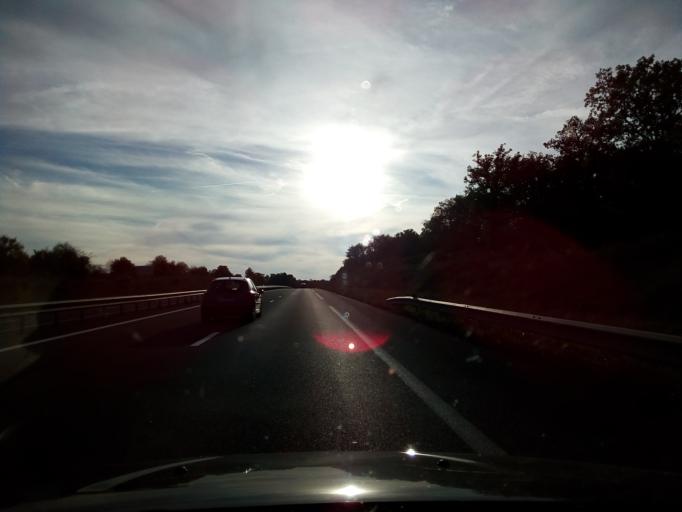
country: FR
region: Poitou-Charentes
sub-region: Departement de la Charente
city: Saint-Projet-Saint-Constant
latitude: 45.7285
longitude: 0.3301
